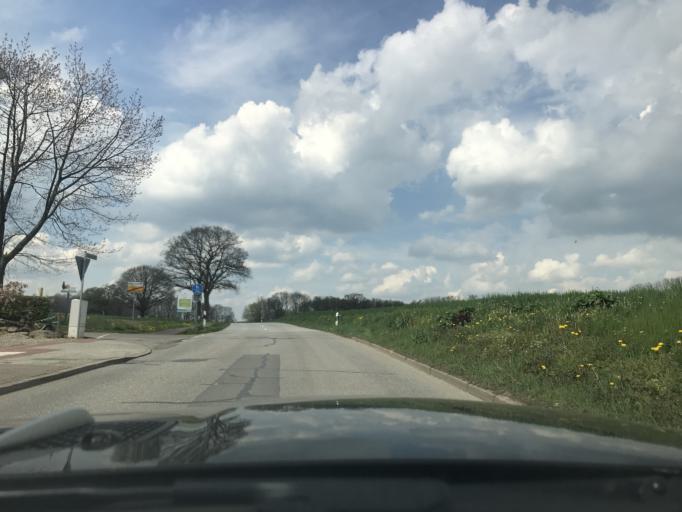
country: DE
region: Schleswig-Holstein
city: Schashagen
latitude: 54.0999
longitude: 10.8817
